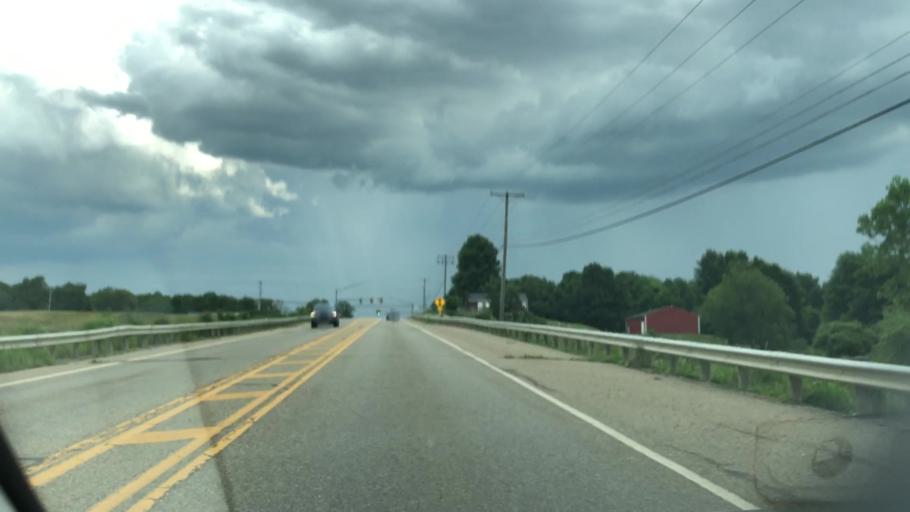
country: US
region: Ohio
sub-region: Summit County
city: Greensburg
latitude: 40.8999
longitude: -81.4431
